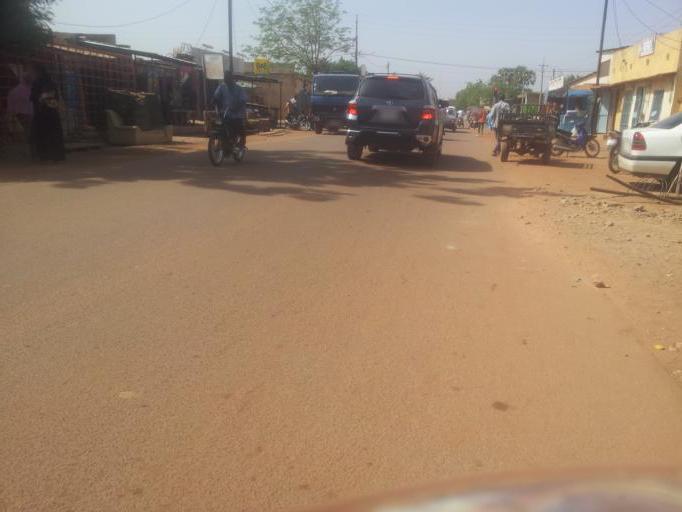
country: BF
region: Centre
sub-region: Kadiogo Province
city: Ouagadougou
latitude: 12.3787
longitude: -1.5398
